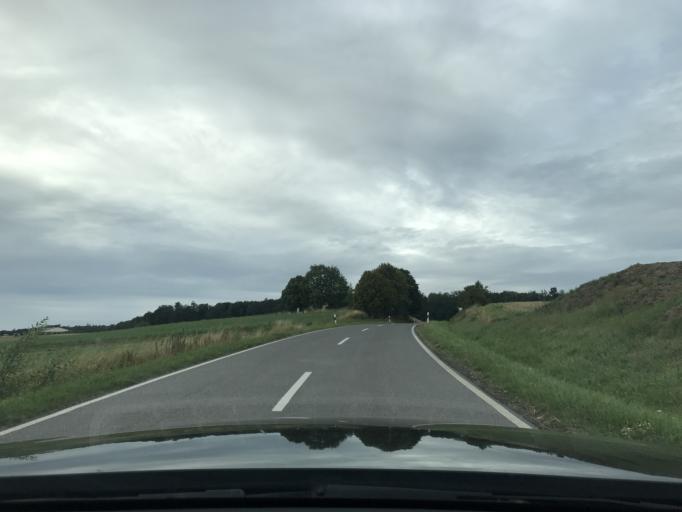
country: DE
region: Bavaria
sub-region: Regierungsbezirk Unterfranken
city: Zeil
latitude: 50.0339
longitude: 10.6360
